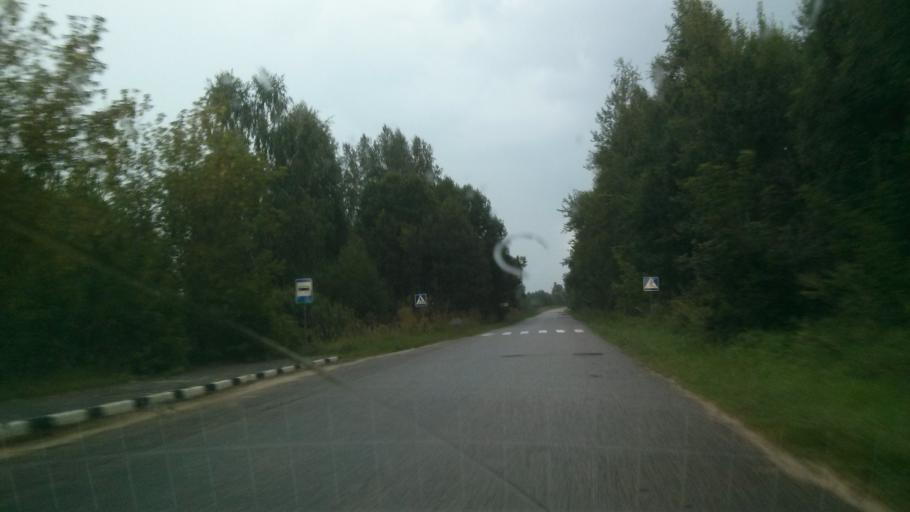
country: RU
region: Nizjnij Novgorod
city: Shimorskoye
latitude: 55.3404
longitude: 41.8613
